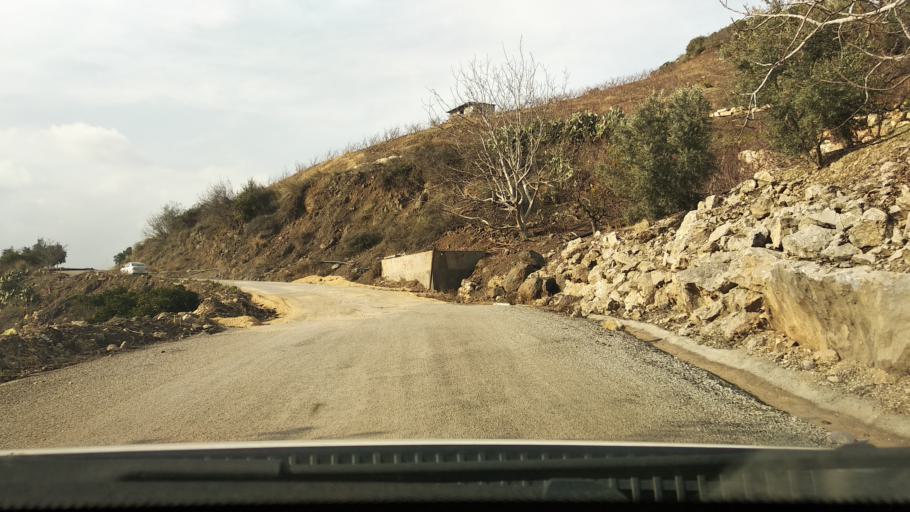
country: TR
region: Mersin
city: Kuzucubelen
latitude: 36.8694
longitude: 34.4703
